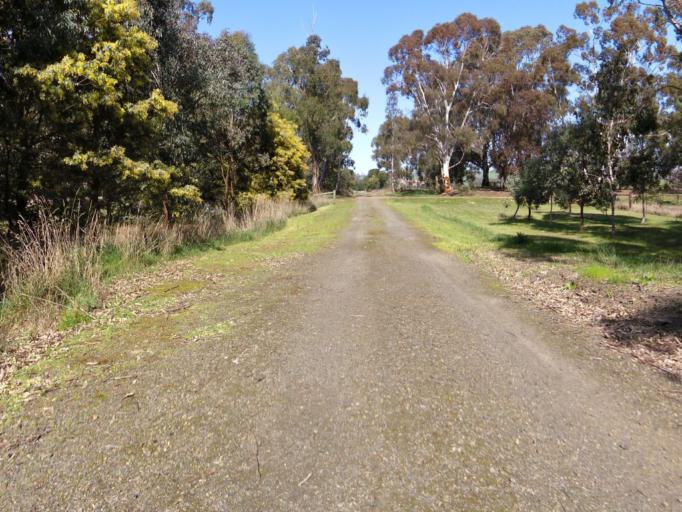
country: AU
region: Victoria
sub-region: Murrindindi
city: Alexandra
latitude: -37.0015
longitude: 145.7462
